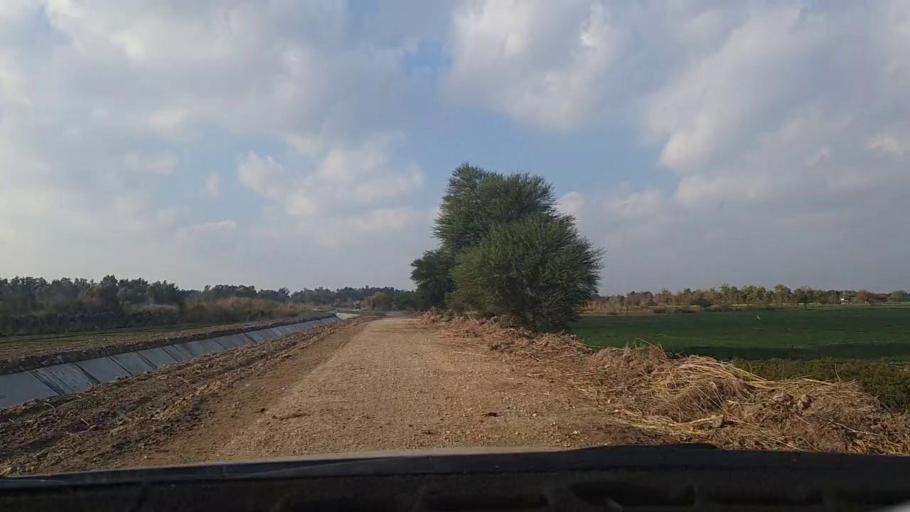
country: PK
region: Sindh
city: Tando Mittha Khan
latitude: 25.9095
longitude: 69.3075
